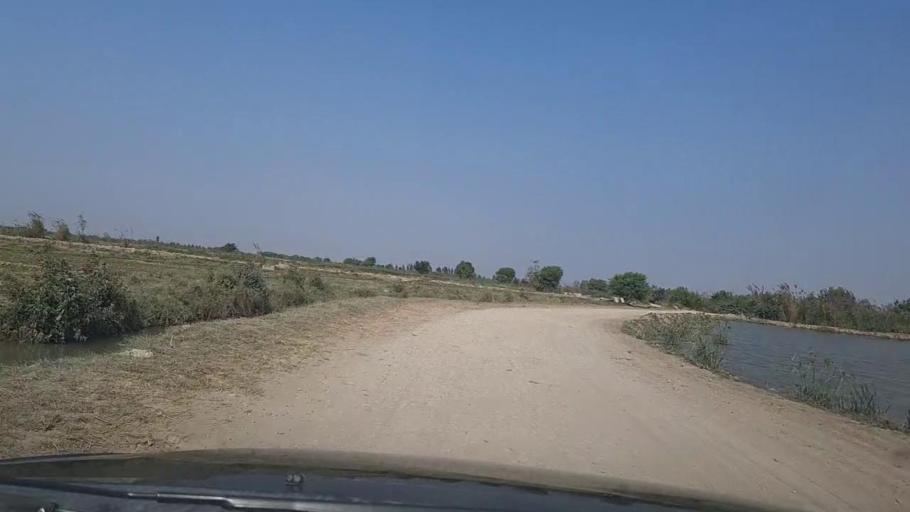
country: PK
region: Sindh
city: Thatta
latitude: 24.6288
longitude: 67.8136
